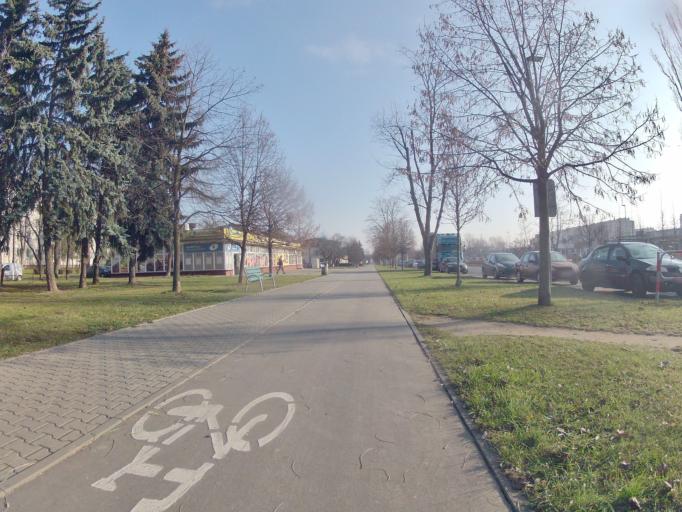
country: PL
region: Lesser Poland Voivodeship
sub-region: Krakow
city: Krakow
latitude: 50.0869
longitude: 20.0094
